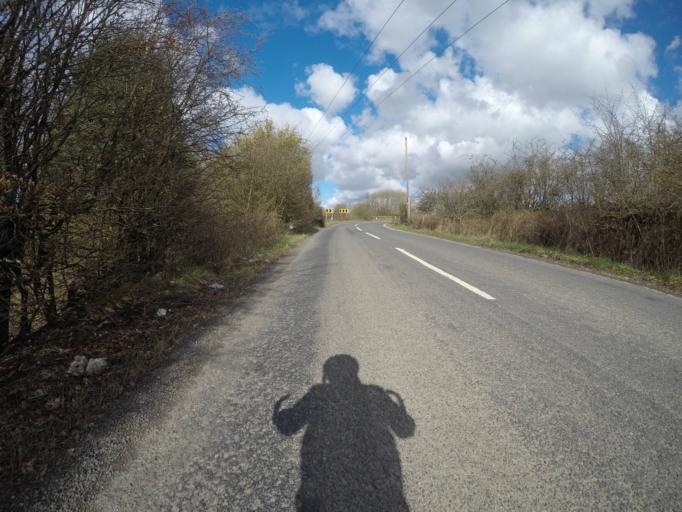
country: GB
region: Scotland
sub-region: North Ayrshire
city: Beith
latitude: 55.7345
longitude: -4.6162
